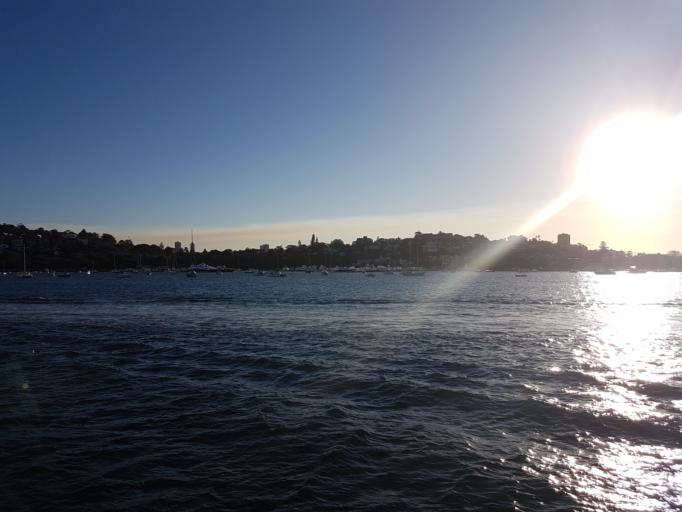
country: AU
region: New South Wales
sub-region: Woollahra
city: Point Piper
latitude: -33.8675
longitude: 151.2624
